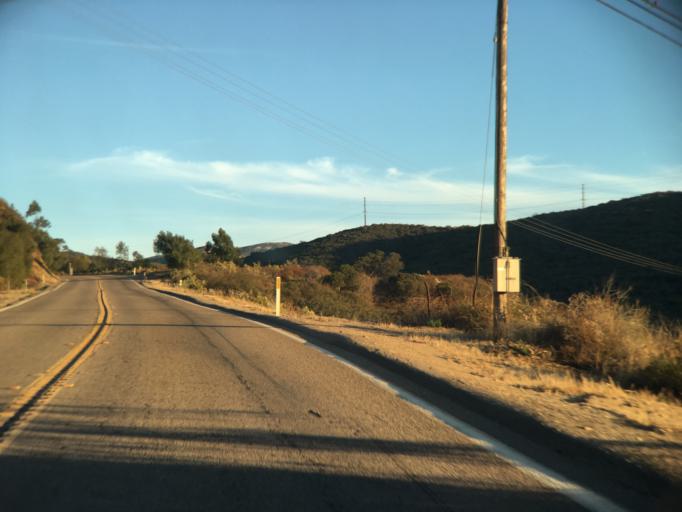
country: US
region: California
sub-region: San Diego County
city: Alpine
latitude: 32.8046
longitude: -116.7805
